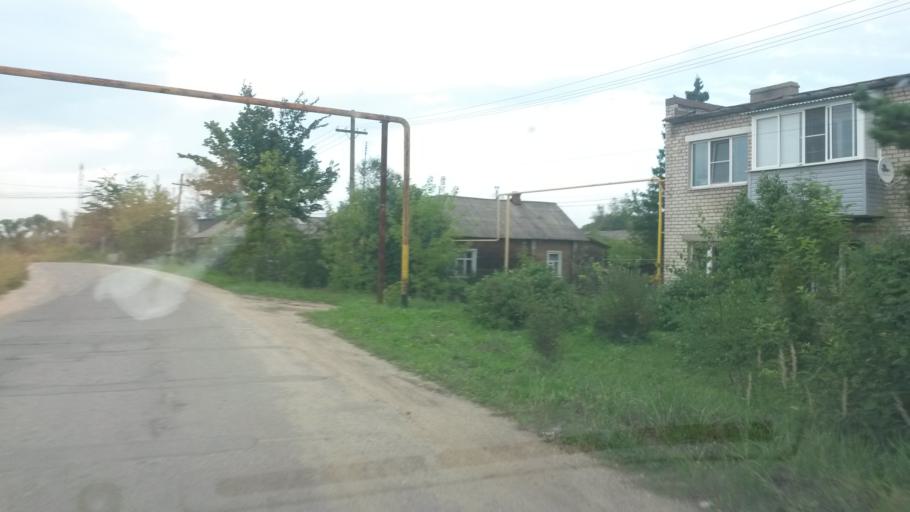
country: RU
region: Jaroslavl
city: Petrovsk
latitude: 56.9980
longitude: 39.2702
